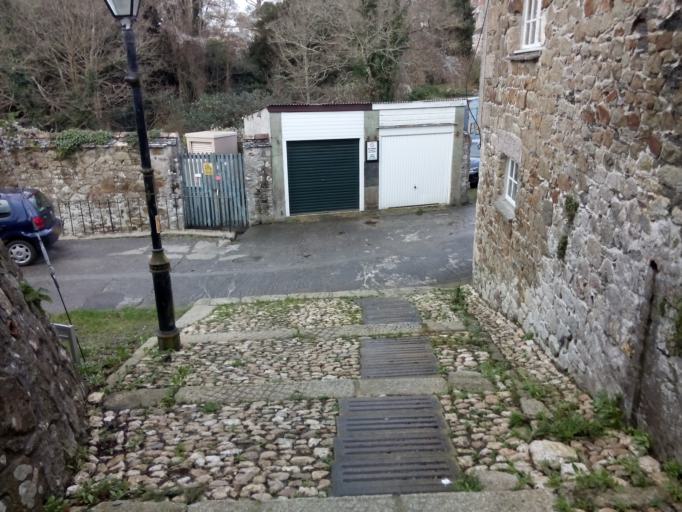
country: GB
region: England
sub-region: Cornwall
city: Helston
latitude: 50.1014
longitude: -5.2753
